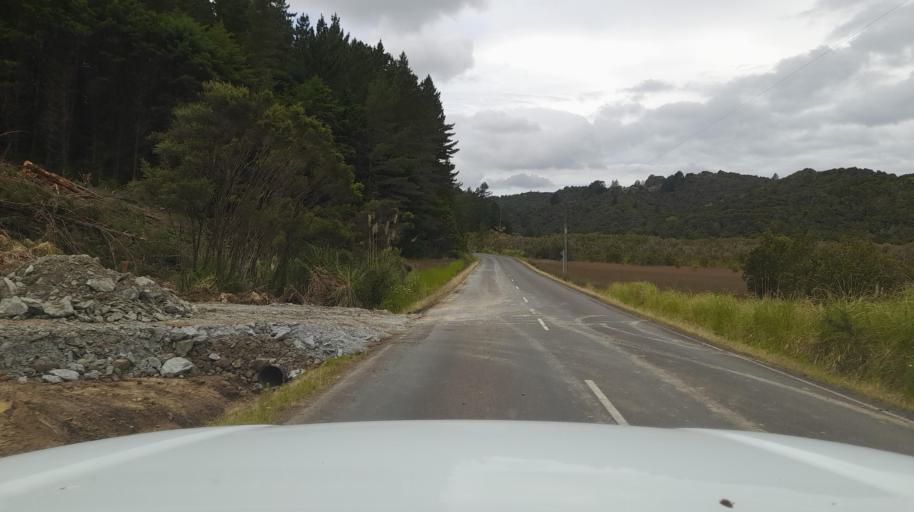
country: NZ
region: Northland
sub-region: Far North District
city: Kaitaia
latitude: -35.3623
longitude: 173.4427
